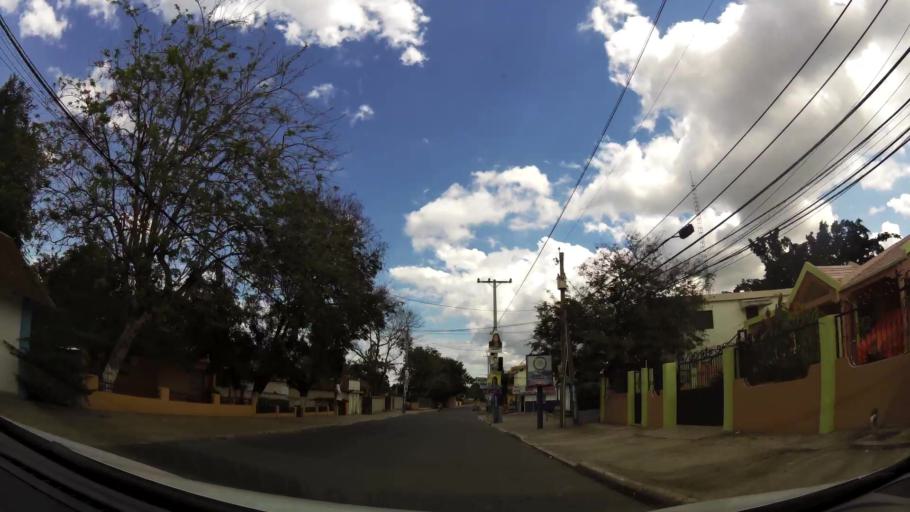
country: DO
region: Santiago
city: Licey al Medio
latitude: 19.3951
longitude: -70.6467
